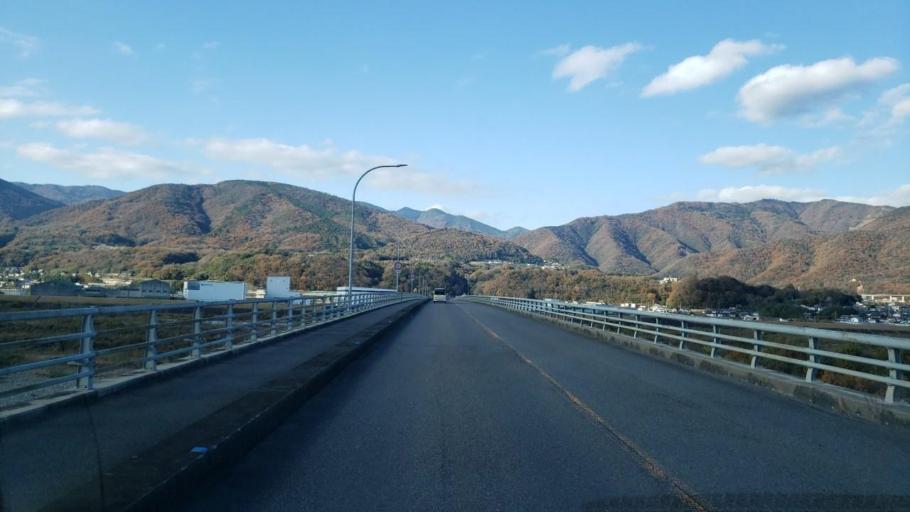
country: JP
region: Tokushima
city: Wakimachi
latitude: 34.0503
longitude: 134.0842
